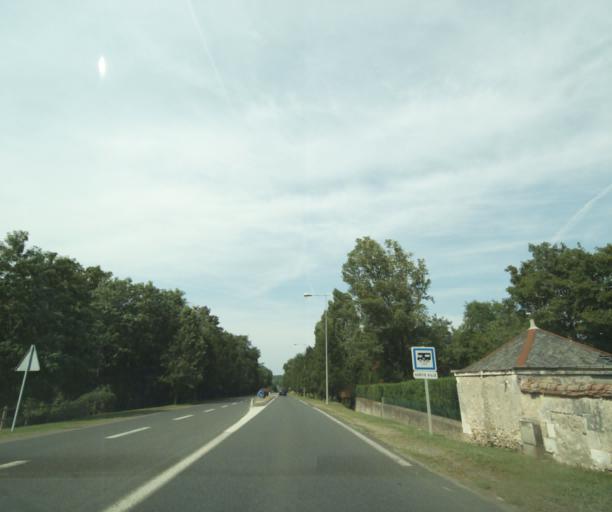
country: FR
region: Centre
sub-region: Departement d'Indre-et-Loire
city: Montbazon
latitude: 47.2796
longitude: 0.7111
